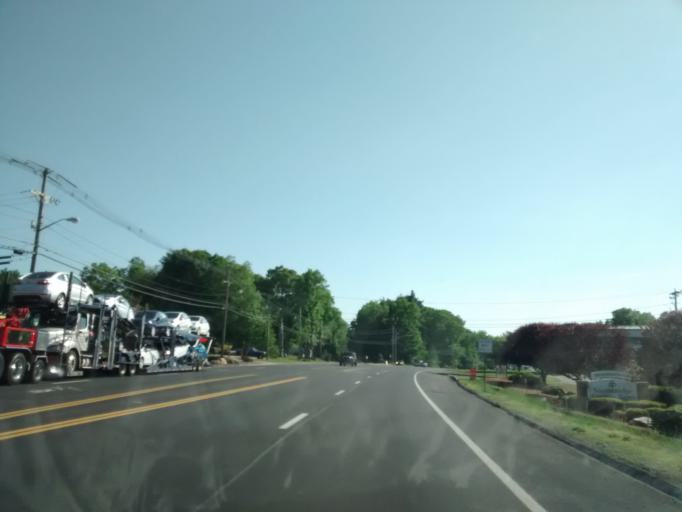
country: US
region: Massachusetts
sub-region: Worcester County
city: Sturbridge
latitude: 42.1186
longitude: -72.0625
